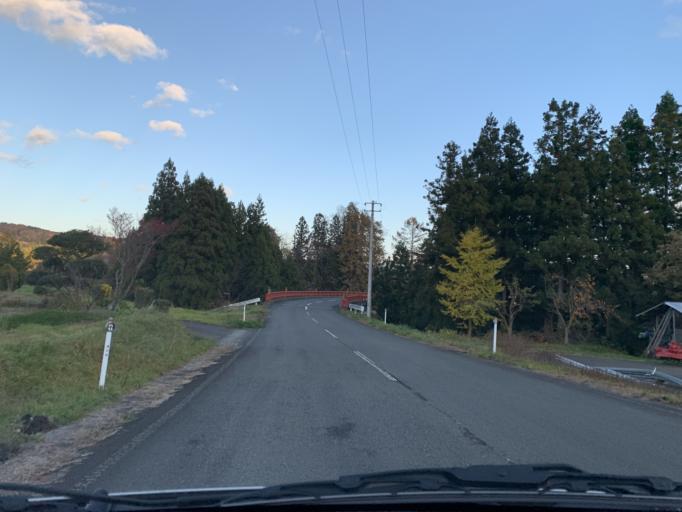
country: JP
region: Iwate
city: Mizusawa
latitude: 39.0429
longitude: 141.0490
